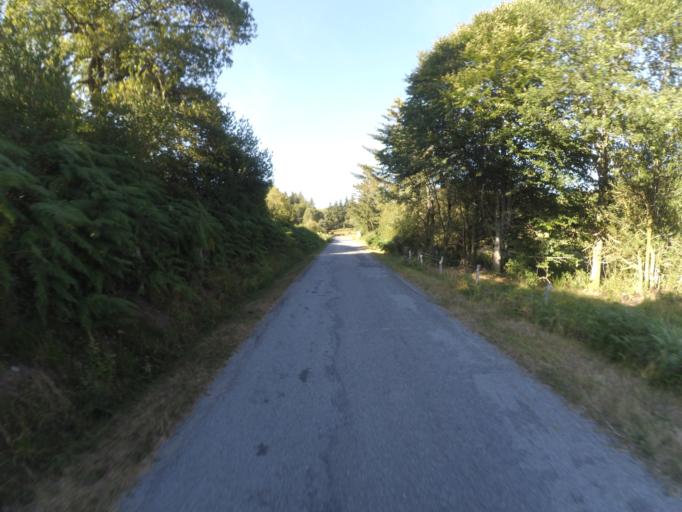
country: FR
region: Limousin
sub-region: Departement de la Creuse
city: Banize
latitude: 45.7579
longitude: 2.0315
